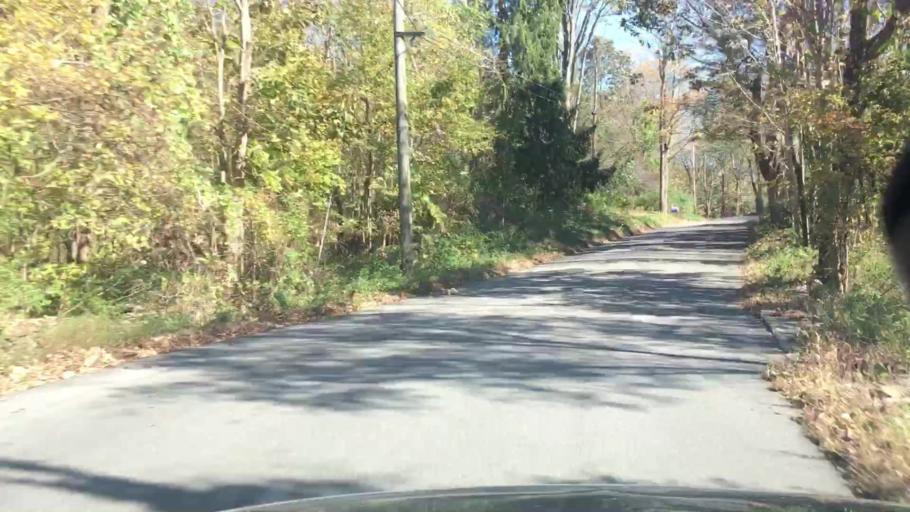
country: US
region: Connecticut
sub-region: Tolland County
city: Stafford
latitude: 41.9900
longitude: -72.2875
